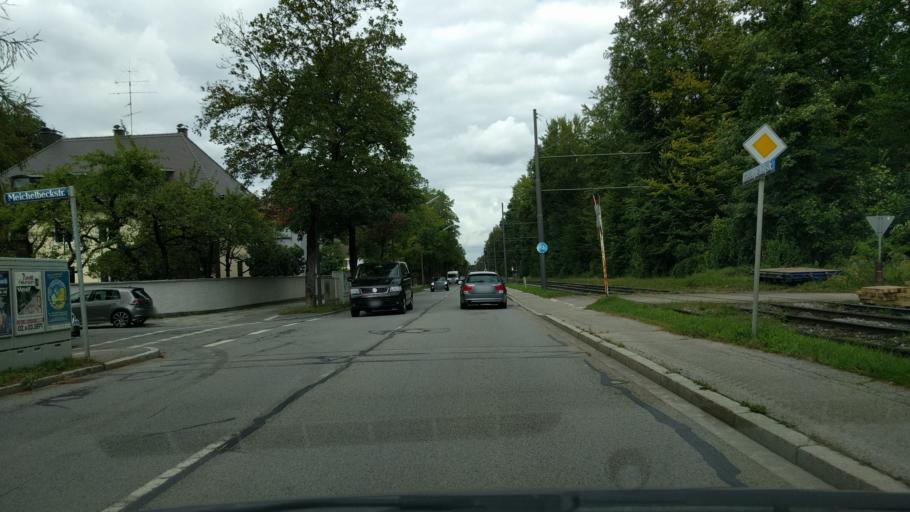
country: DE
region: Bavaria
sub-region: Upper Bavaria
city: Pullach im Isartal
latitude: 48.0784
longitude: 11.5508
